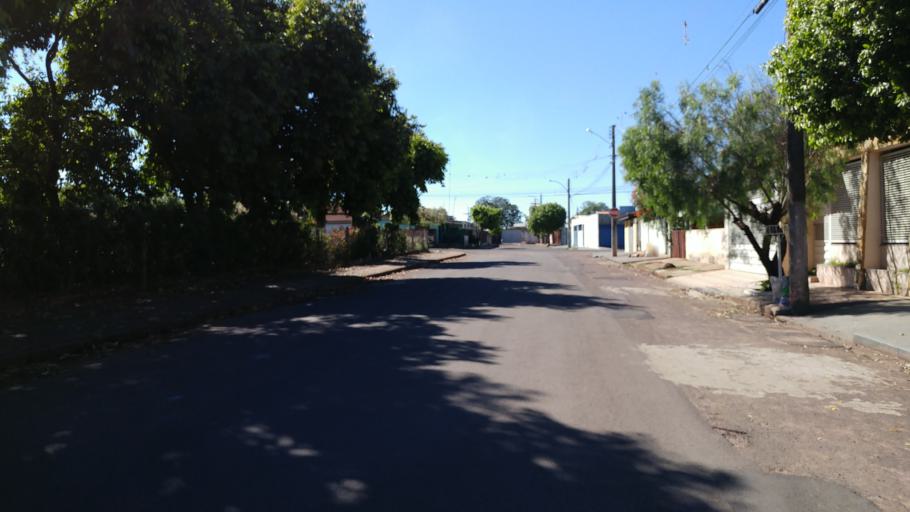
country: BR
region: Sao Paulo
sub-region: Paraguacu Paulista
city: Paraguacu Paulista
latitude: -22.4191
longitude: -50.5828
